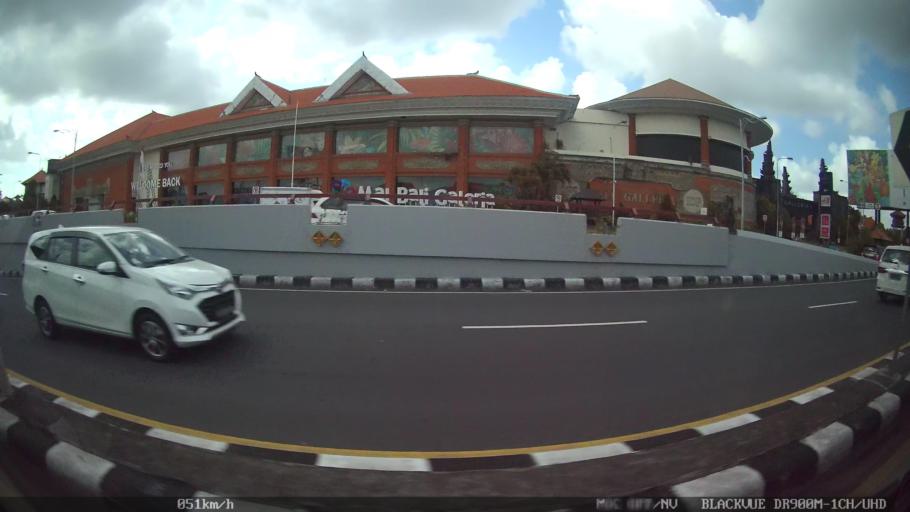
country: ID
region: Bali
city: Jabajero
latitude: -8.7227
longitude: 115.1812
